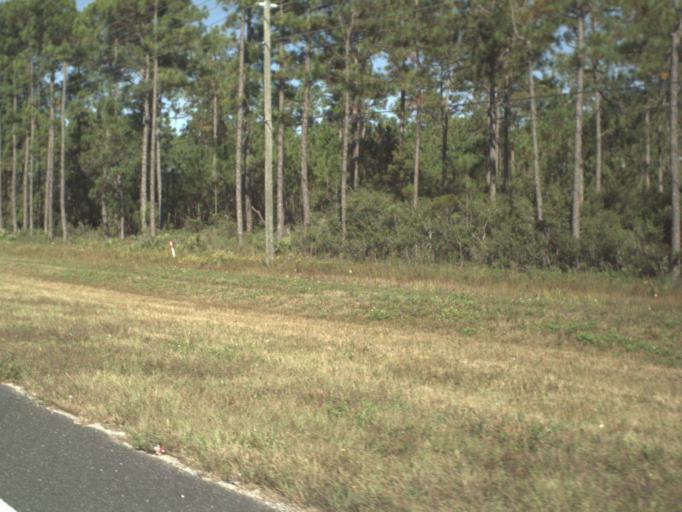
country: US
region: Florida
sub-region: Walton County
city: Seaside
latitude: 30.3688
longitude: -86.1923
